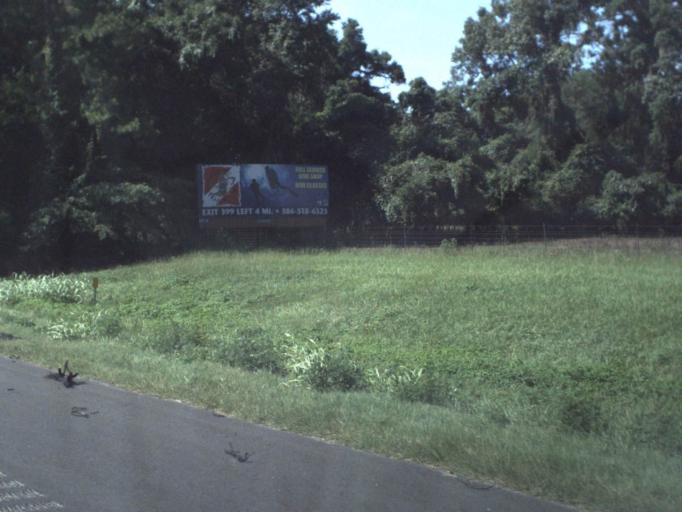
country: US
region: Florida
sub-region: Alachua County
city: High Springs
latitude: 29.8242
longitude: -82.5199
